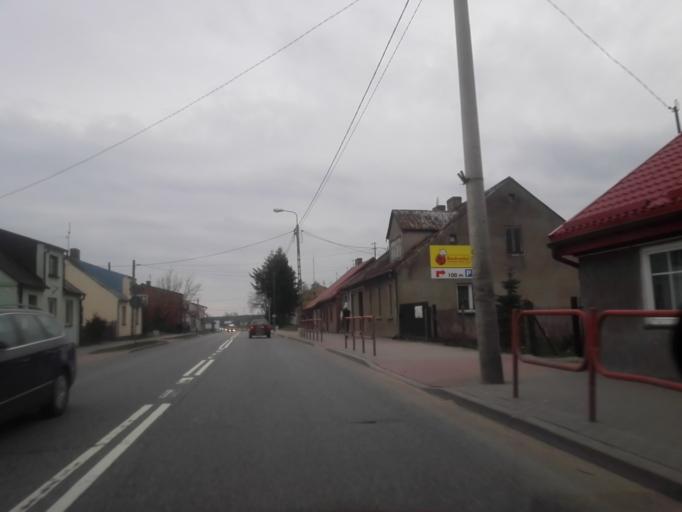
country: PL
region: Podlasie
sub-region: Powiat grajewski
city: Rajgrod
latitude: 53.7294
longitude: 22.6887
